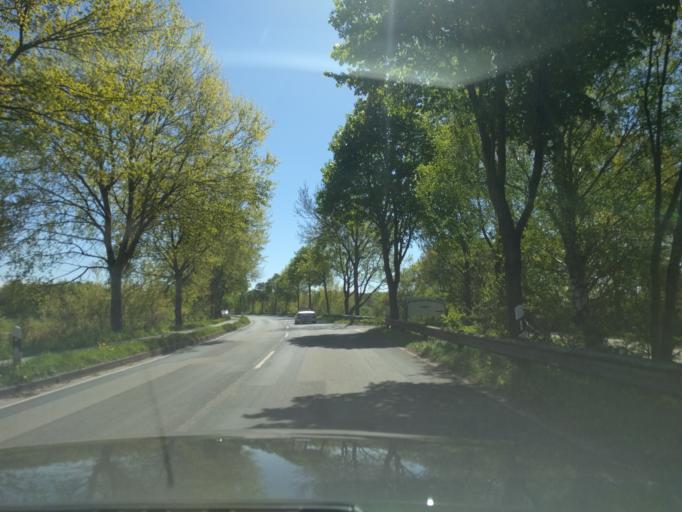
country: DE
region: Lower Saxony
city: Seevetal
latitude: 53.3901
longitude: 10.0145
